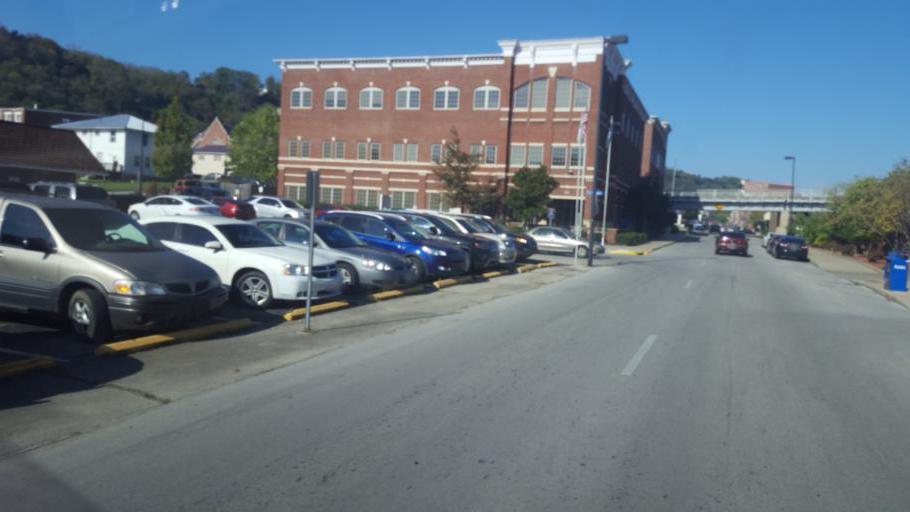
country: US
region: Ohio
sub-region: Brown County
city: Aberdeen
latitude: 38.6460
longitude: -83.7605
